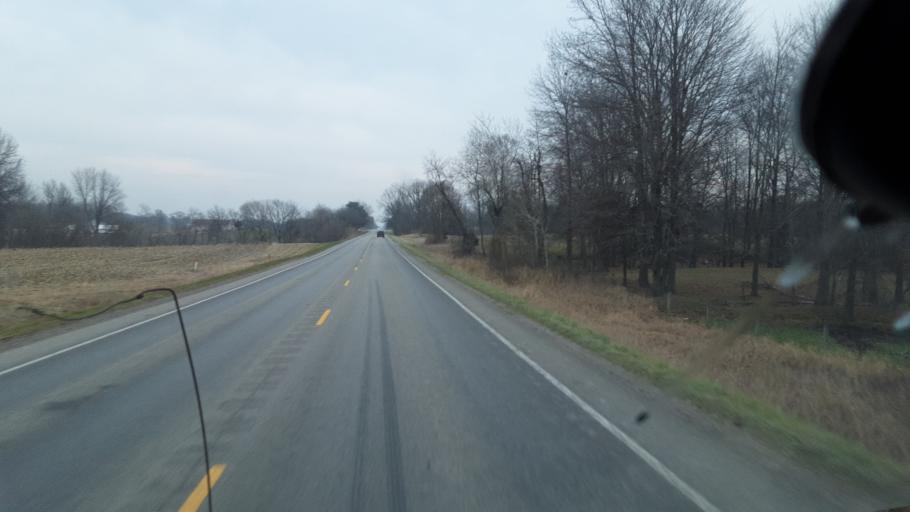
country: US
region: Michigan
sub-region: Saint Joseph County
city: White Pigeon
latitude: 41.7263
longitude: -85.6273
